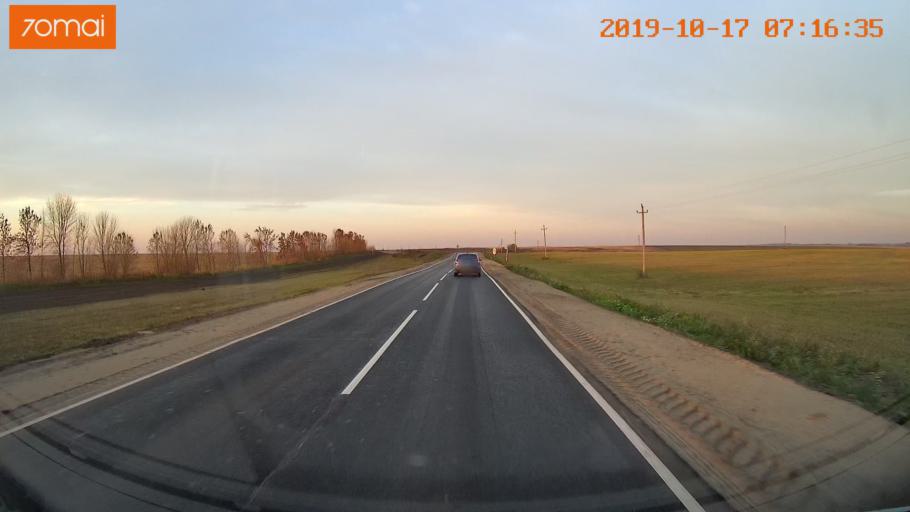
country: RU
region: Vladimir
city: Suzdal'
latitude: 56.3713
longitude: 40.2460
